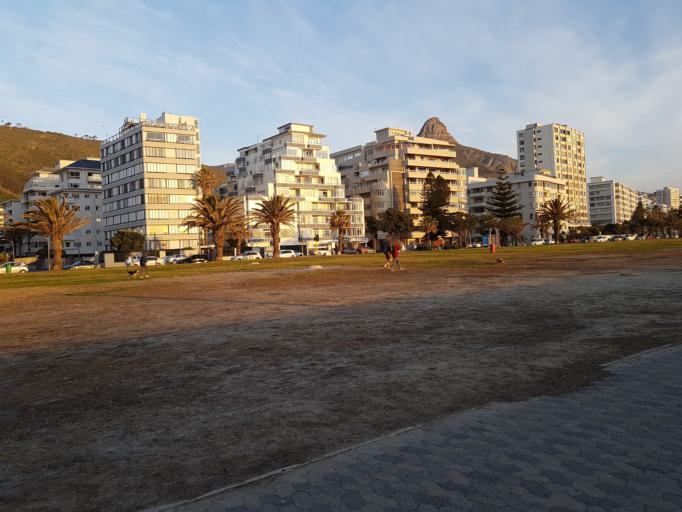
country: ZA
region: Western Cape
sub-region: City of Cape Town
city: Cape Town
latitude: -33.9102
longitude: 18.3896
